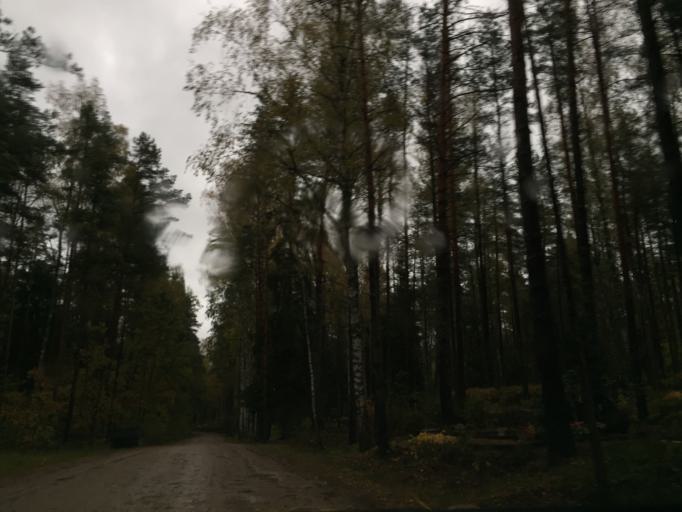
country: LV
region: Engure
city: Smarde
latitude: 56.9274
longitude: 23.4744
